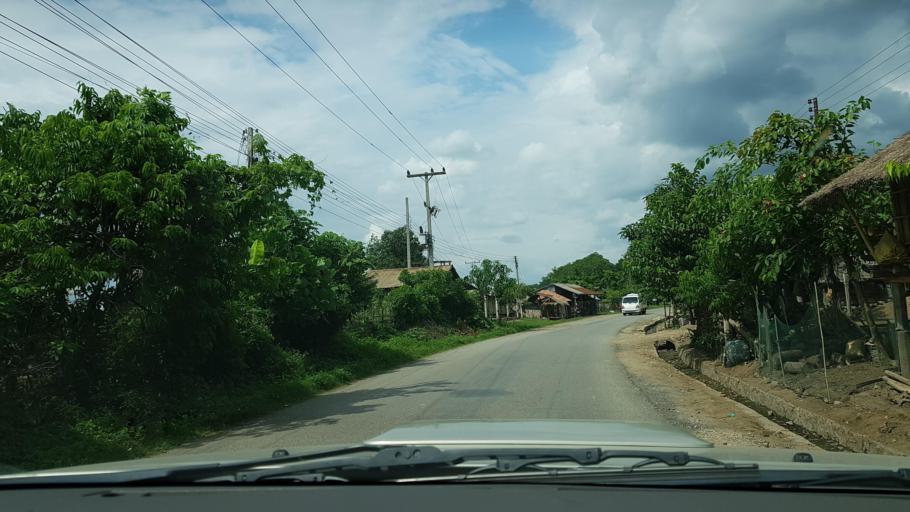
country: LA
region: Loungnamtha
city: Muang Nale
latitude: 20.2720
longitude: 101.6030
